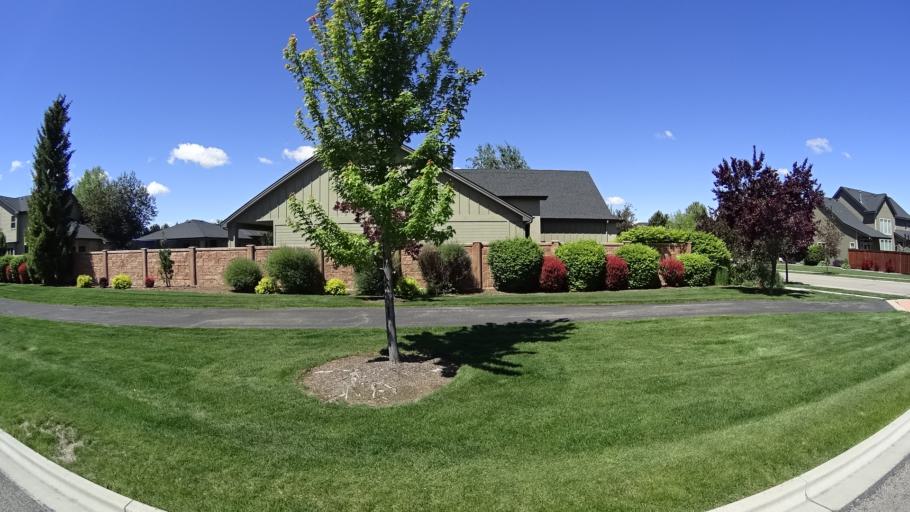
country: US
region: Idaho
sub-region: Ada County
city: Meridian
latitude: 43.6536
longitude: -116.3847
